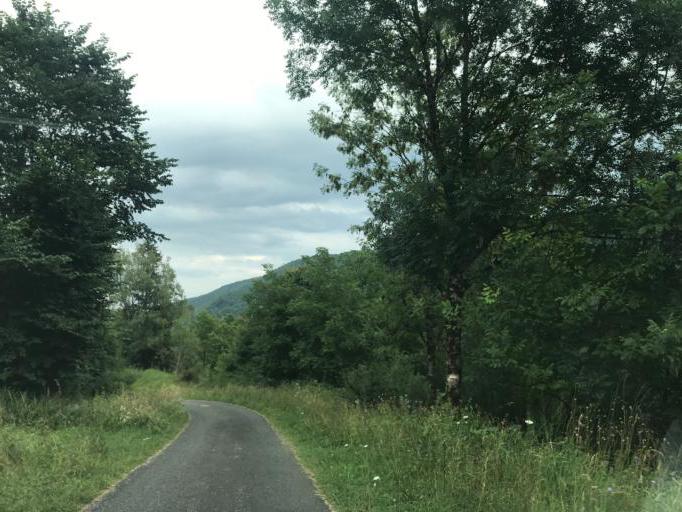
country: FR
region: Franche-Comte
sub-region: Departement du Jura
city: Longchaumois
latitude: 46.4671
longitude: 5.8945
